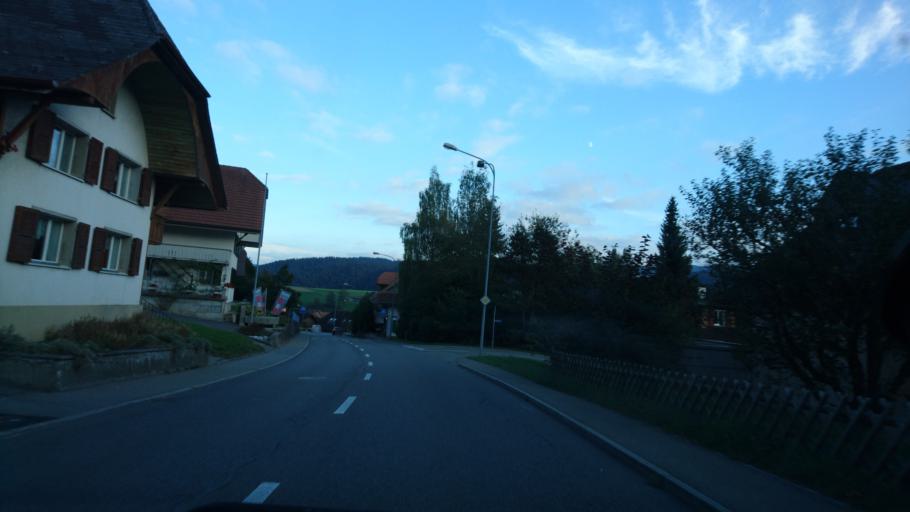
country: CH
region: Bern
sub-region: Bern-Mittelland District
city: Zaziwil
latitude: 46.9027
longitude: 7.6557
